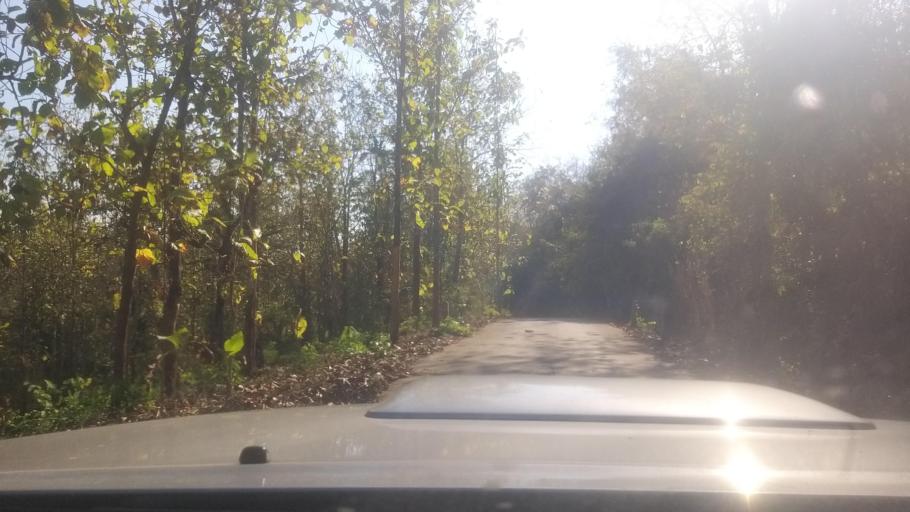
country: TH
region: Phrae
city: Phrae
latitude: 18.2725
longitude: 99.9882
